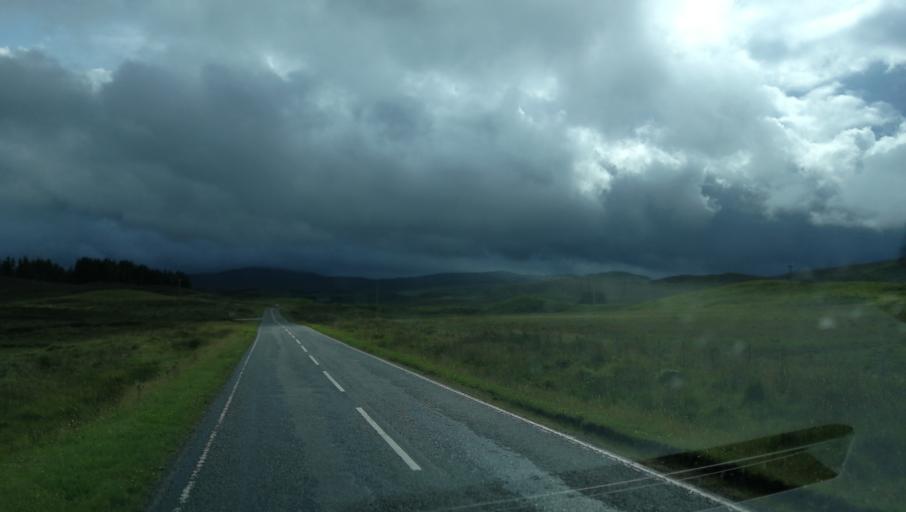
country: GB
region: Scotland
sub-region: Highland
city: Ullapool
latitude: 58.0785
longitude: -4.9740
